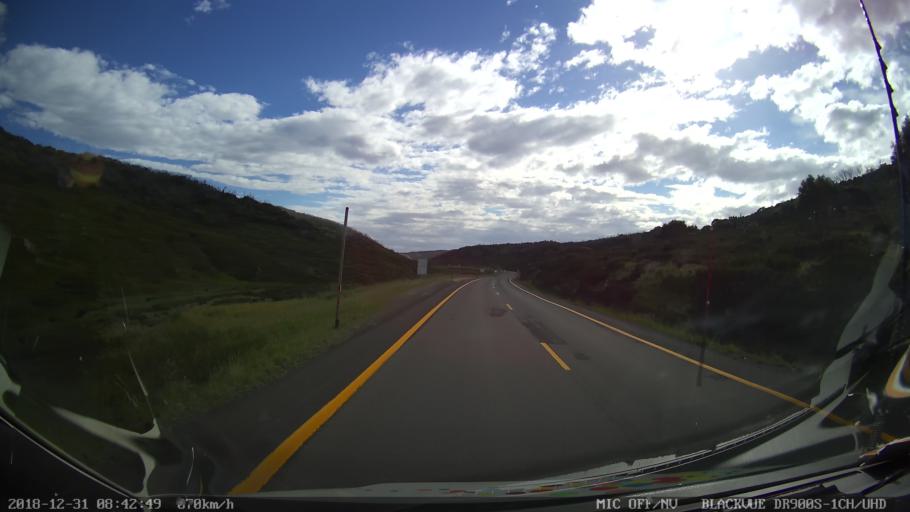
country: AU
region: New South Wales
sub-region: Snowy River
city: Jindabyne
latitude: -36.3923
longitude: 148.4373
